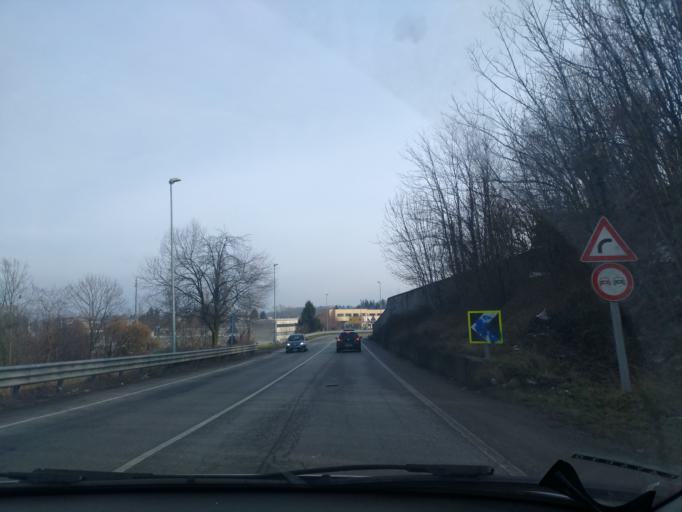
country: IT
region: Lombardy
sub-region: Provincia di Como
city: Anzano del Parco
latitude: 45.7645
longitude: 9.2009
